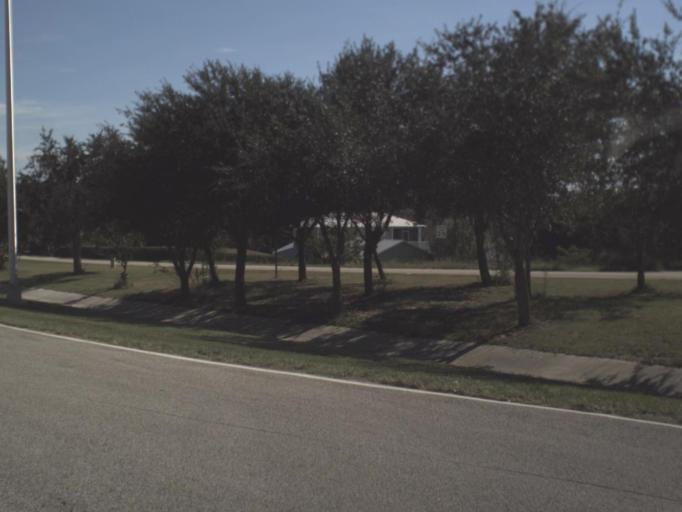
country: US
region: Florida
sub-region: Highlands County
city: Lake Placid
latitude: 27.3181
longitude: -81.3637
